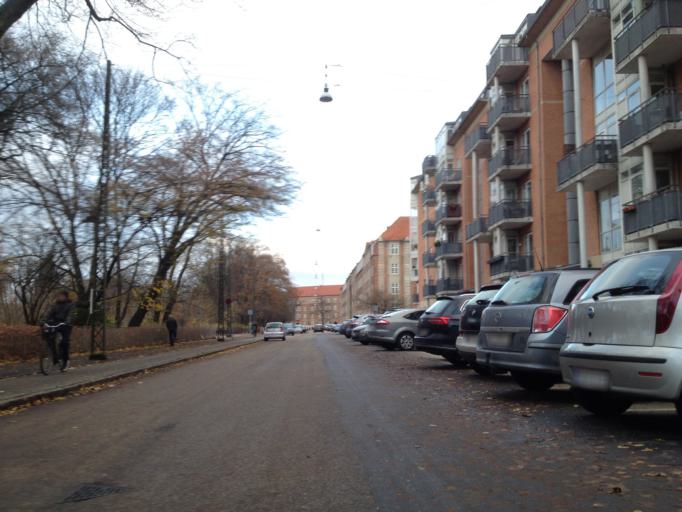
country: DK
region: Capital Region
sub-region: Kobenhavn
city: Copenhagen
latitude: 55.7060
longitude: 12.5733
